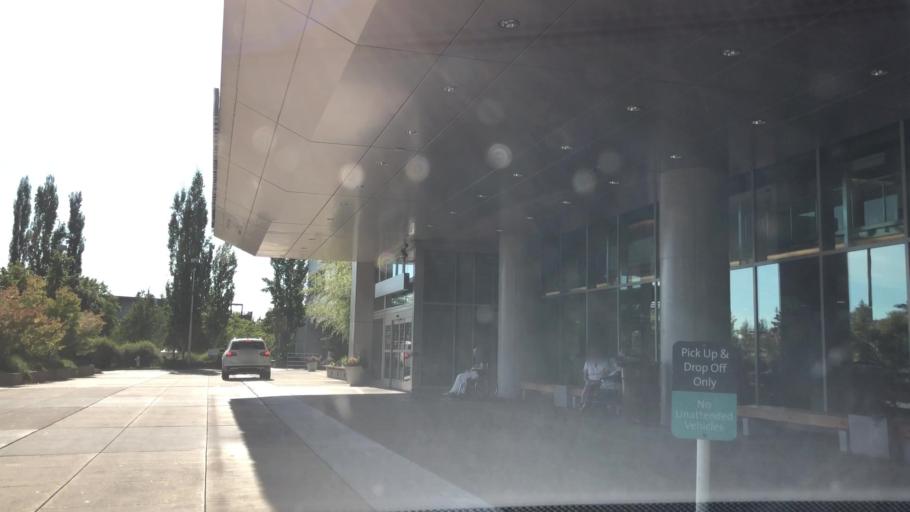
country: US
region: Washington
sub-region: King County
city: Kingsgate
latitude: 47.7155
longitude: -122.1793
